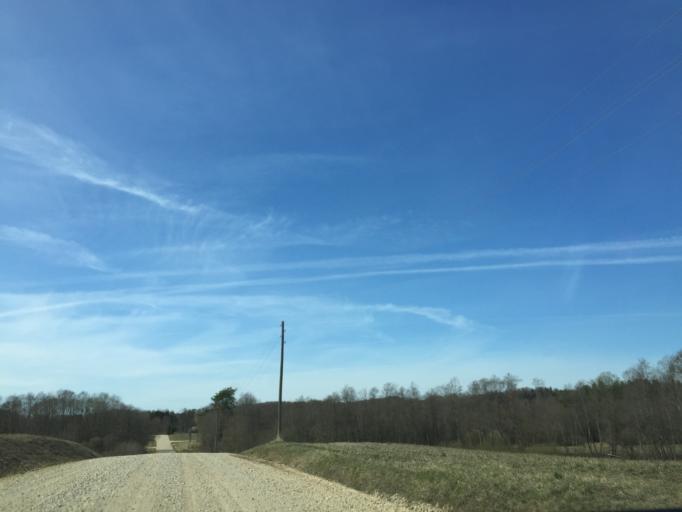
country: EE
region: Vorumaa
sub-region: Antsla vald
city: Vana-Antsla
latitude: 57.9546
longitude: 26.3618
